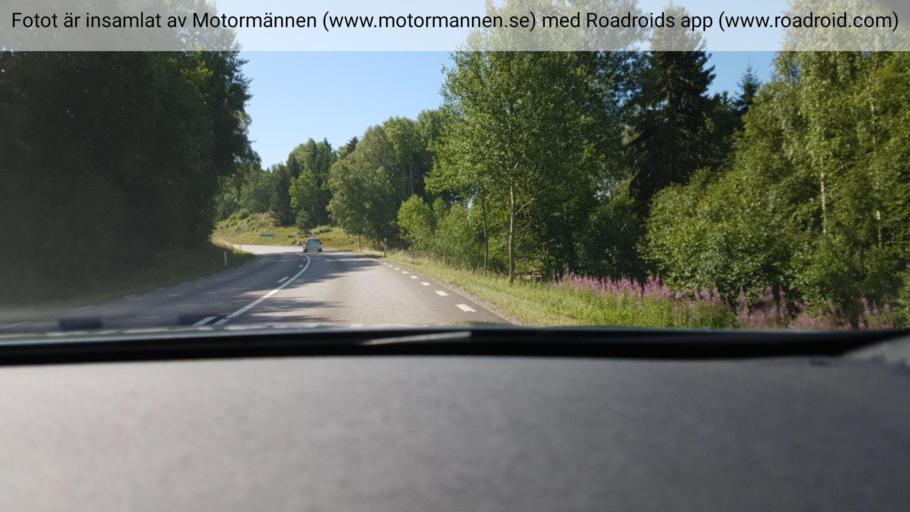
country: SE
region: Joenkoeping
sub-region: Mullsjo Kommun
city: Mullsjoe
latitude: 58.0538
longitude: 13.8044
